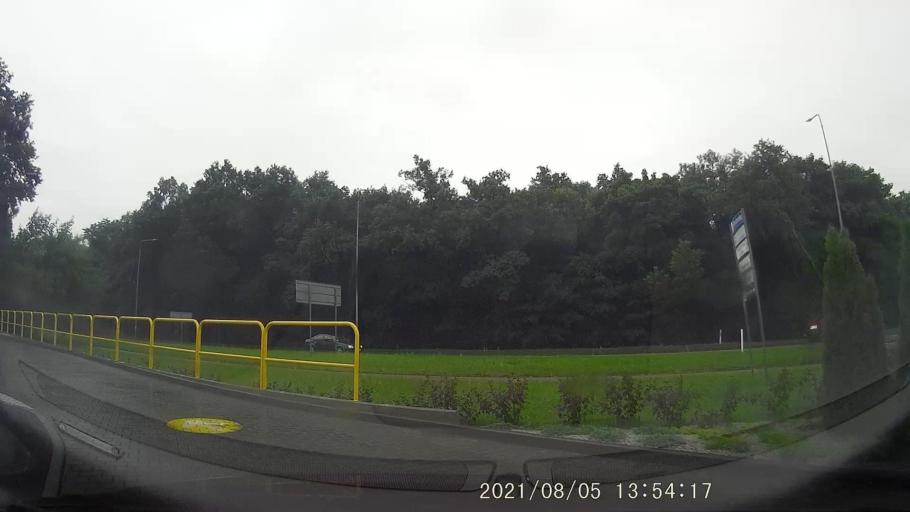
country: PL
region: Opole Voivodeship
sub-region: Powiat krapkowicki
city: Krapkowice
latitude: 50.4686
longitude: 17.9554
